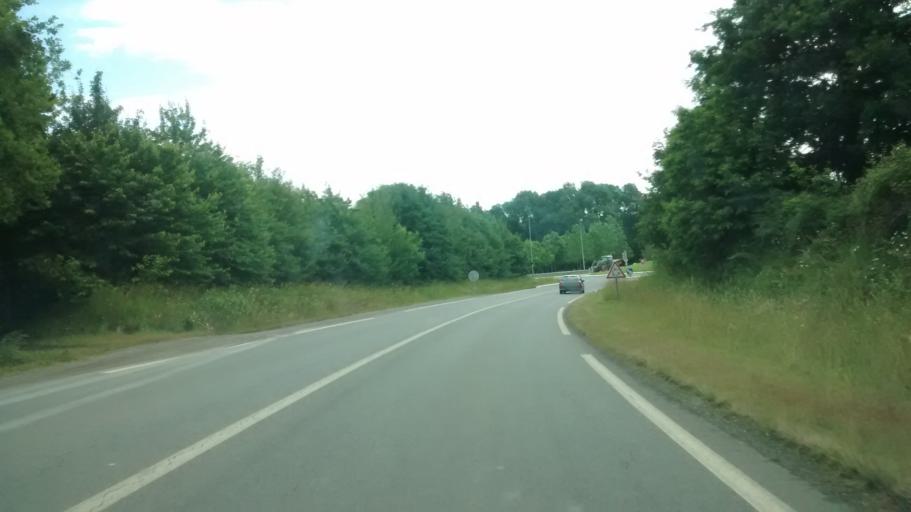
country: FR
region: Brittany
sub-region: Departement du Morbihan
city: La Gacilly
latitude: 47.7743
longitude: -2.1245
